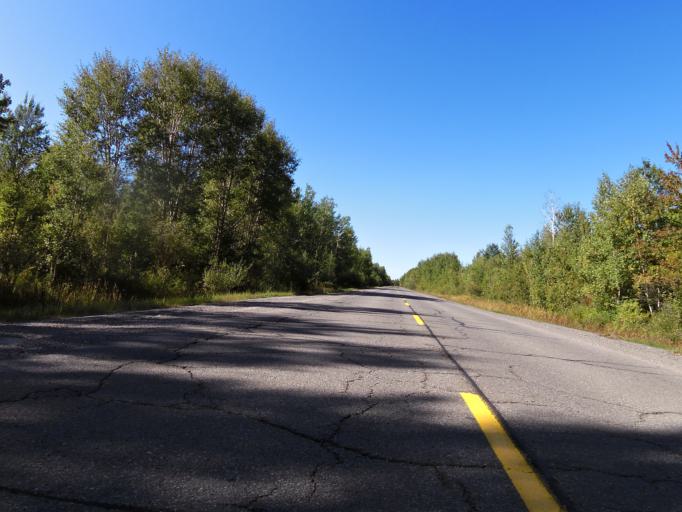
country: CA
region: Ontario
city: Clarence-Rockland
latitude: 45.3314
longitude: -75.4220
